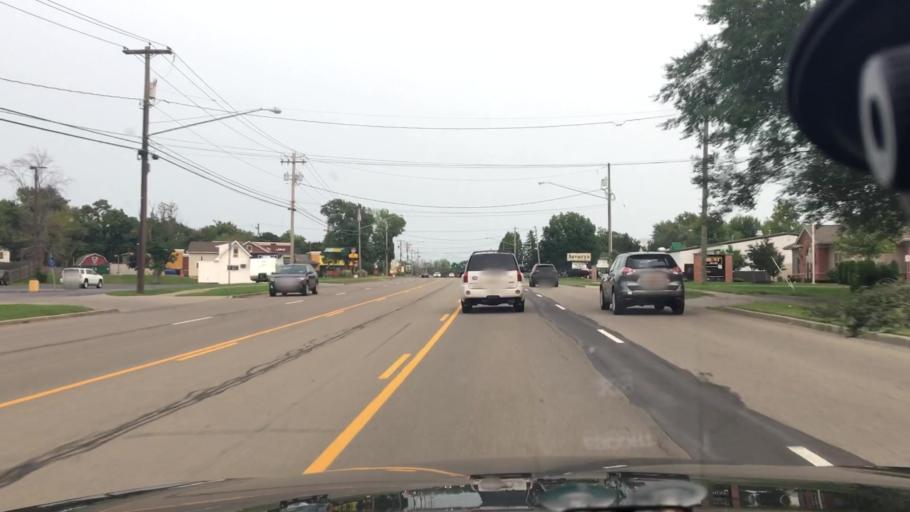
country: US
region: New York
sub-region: Erie County
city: Hamburg
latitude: 42.7364
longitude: -78.8421
